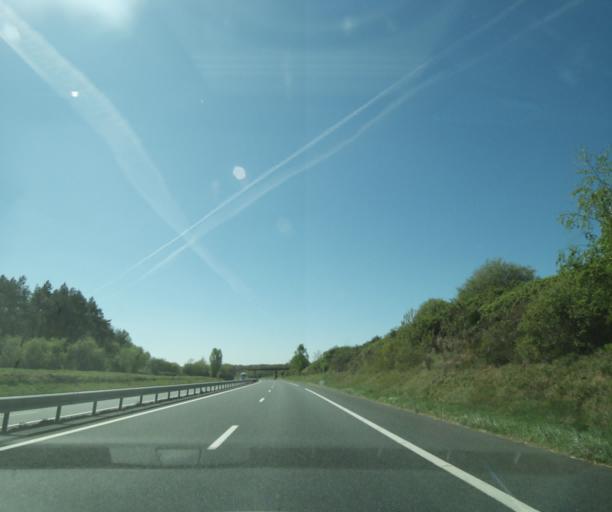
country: FR
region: Centre
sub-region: Departement de l'Indre
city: Chantome
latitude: 46.4123
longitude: 1.4640
